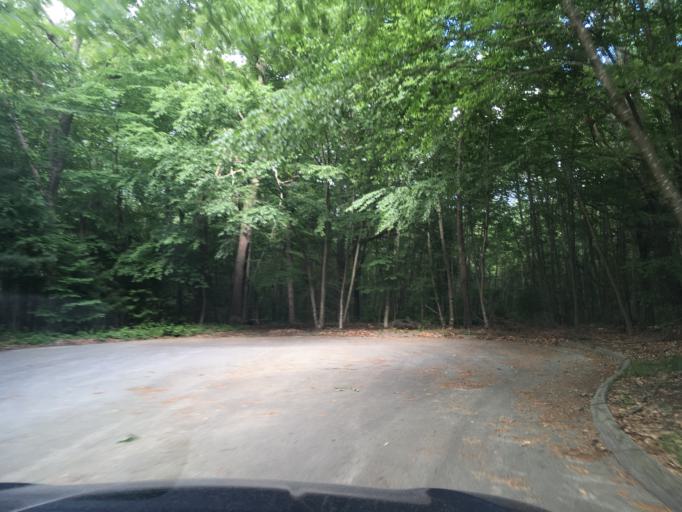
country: US
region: Rhode Island
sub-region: Washington County
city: Exeter
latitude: 41.6321
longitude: -71.5379
